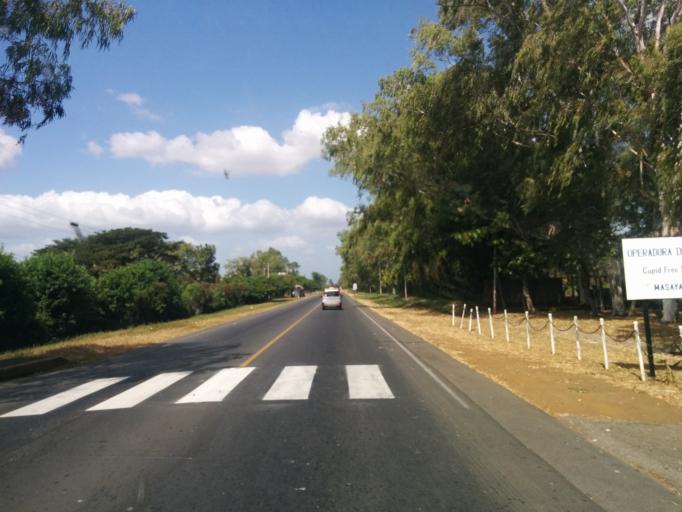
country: NI
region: Masaya
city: Nindiri
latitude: 12.0013
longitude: -86.1041
